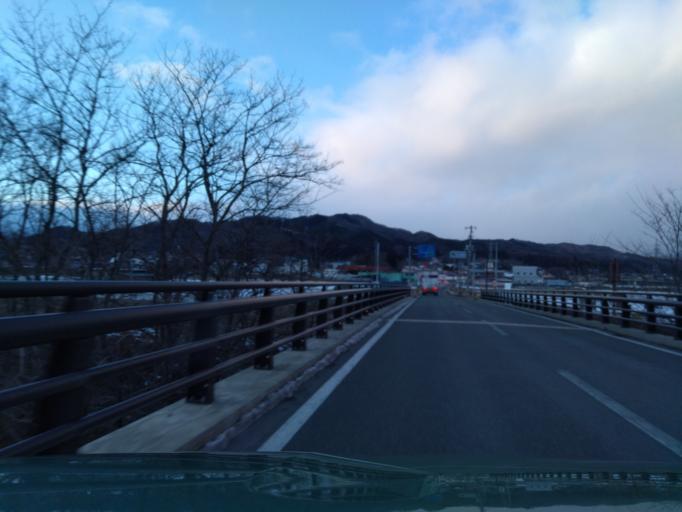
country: JP
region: Iwate
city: Shizukuishi
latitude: 39.6971
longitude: 141.0637
